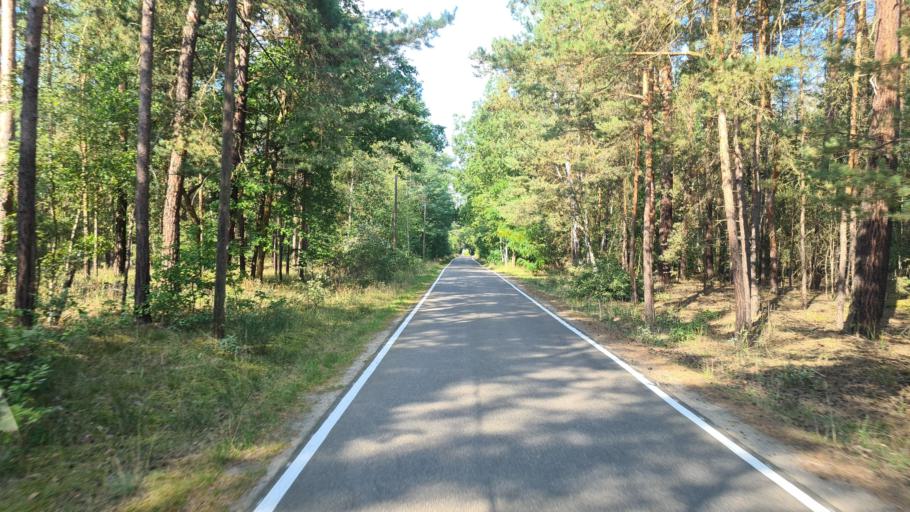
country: DE
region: Brandenburg
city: Drebkau
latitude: 51.6927
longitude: 14.1836
